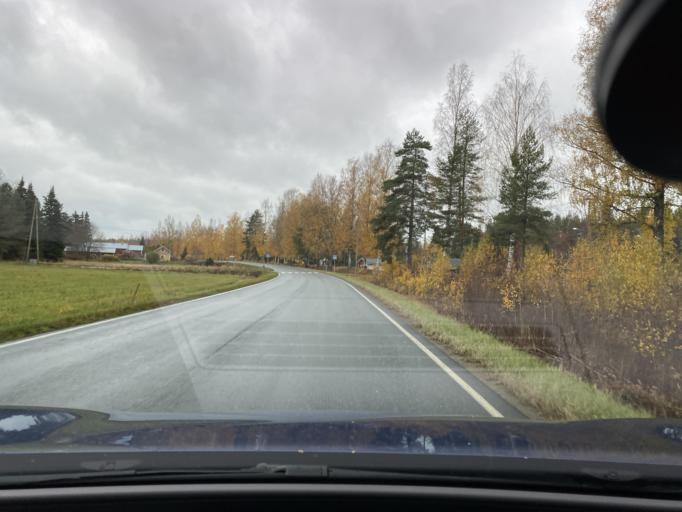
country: FI
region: Satakunta
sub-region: Pori
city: Kokemaeki
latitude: 61.2652
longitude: 22.4029
